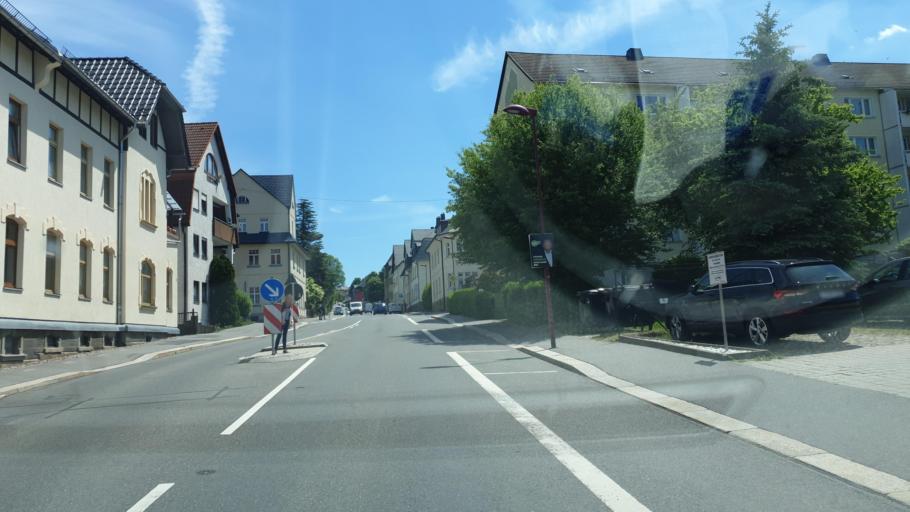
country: DE
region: Saxony
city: Rodewisch
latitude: 50.5294
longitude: 12.4079
